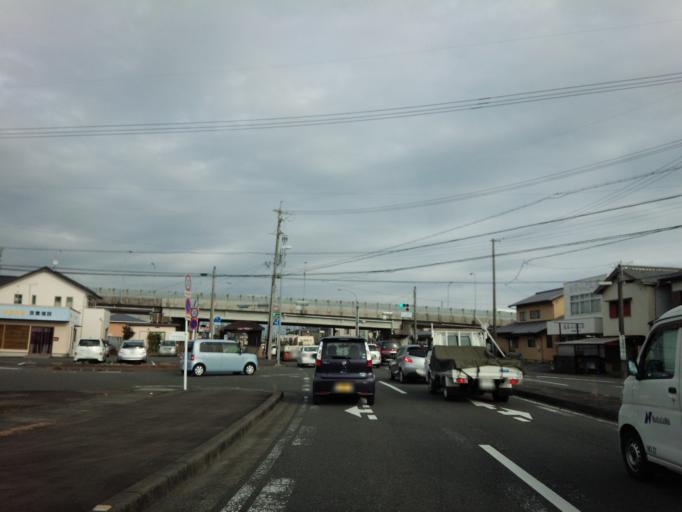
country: JP
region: Shizuoka
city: Yaizu
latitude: 34.8631
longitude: 138.2998
